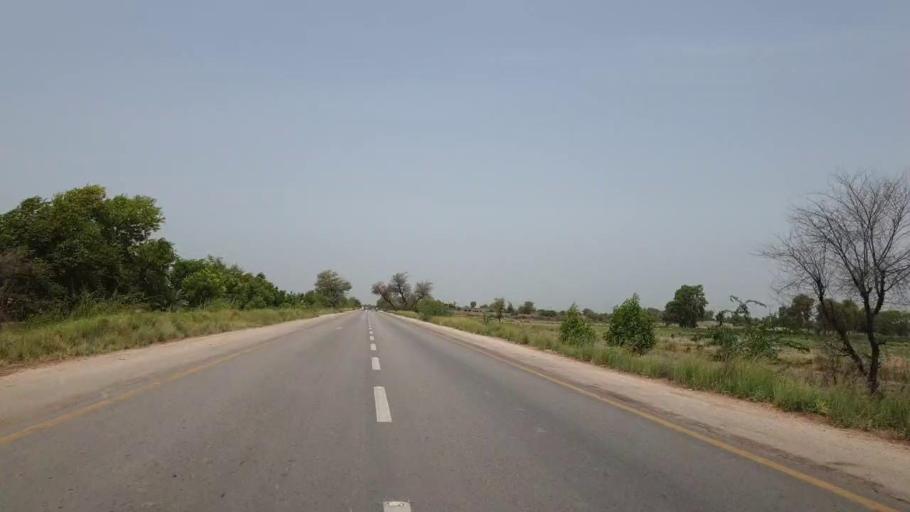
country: PK
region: Sindh
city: Nawabshah
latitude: 26.2122
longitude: 68.5159
